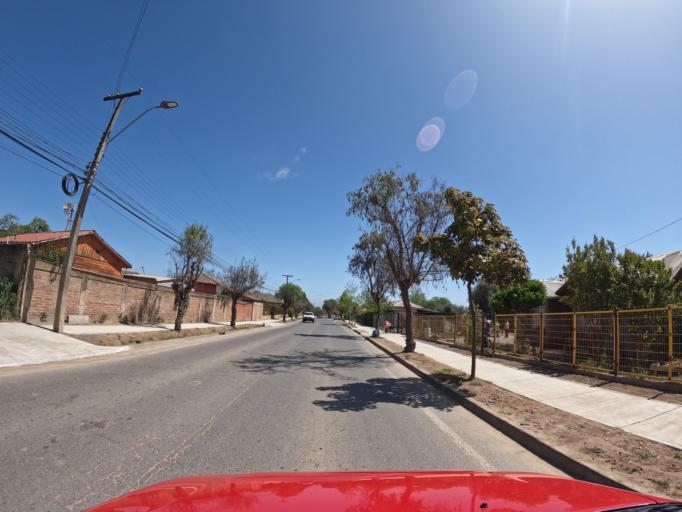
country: CL
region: O'Higgins
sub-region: Provincia de Colchagua
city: Santa Cruz
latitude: -34.7291
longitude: -71.6545
